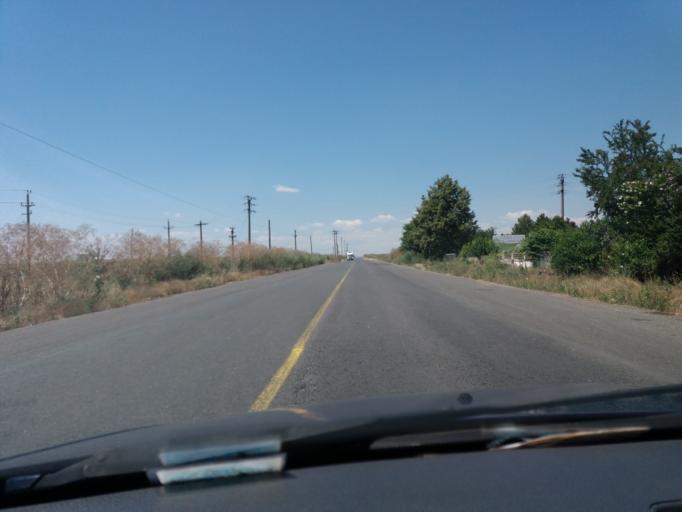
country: RO
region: Constanta
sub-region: Comuna Lumina
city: Lumina
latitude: 44.2863
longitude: 28.5903
